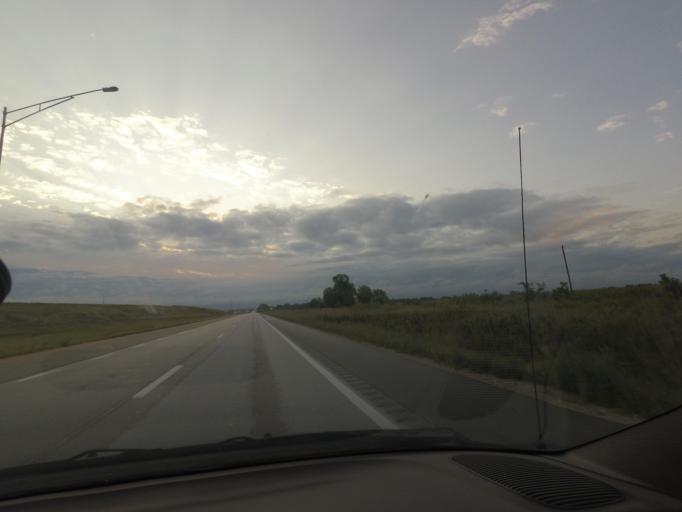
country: US
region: Missouri
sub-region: Shelby County
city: Shelbina
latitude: 39.7052
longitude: -92.0892
